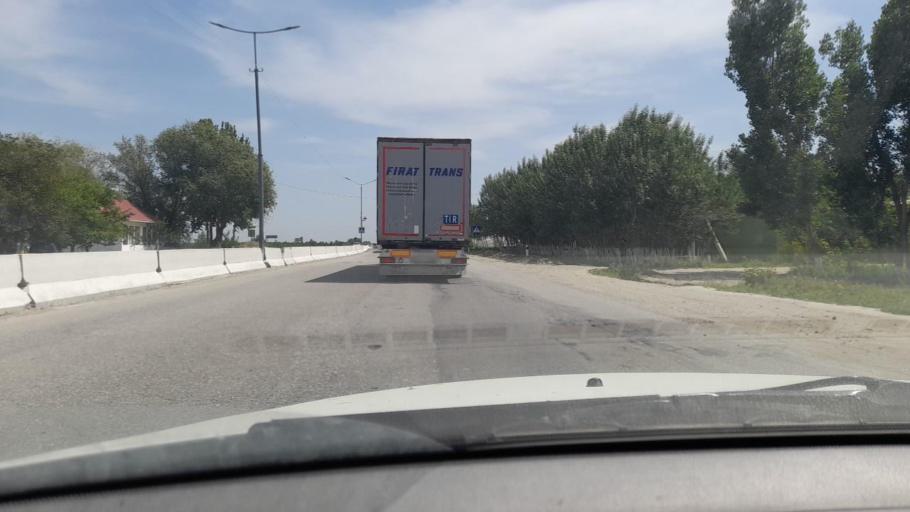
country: UZ
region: Navoiy
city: Navoiy
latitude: 40.0792
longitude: 65.6096
